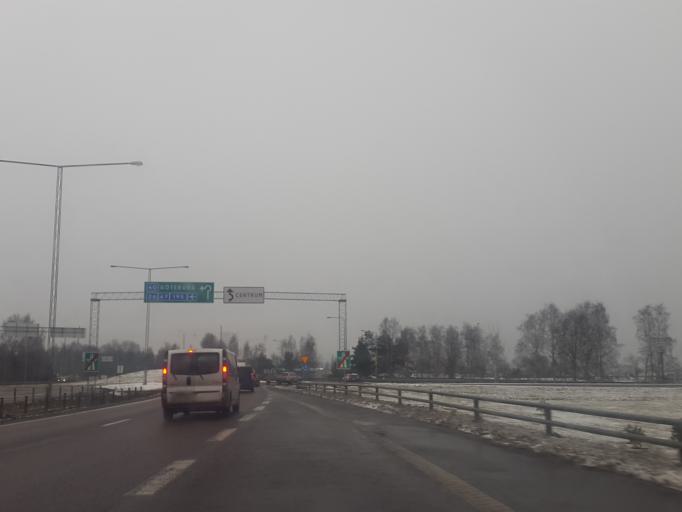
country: SE
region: Joenkoeping
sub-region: Jonkopings Kommun
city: Jonkoping
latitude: 57.7587
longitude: 14.1572
